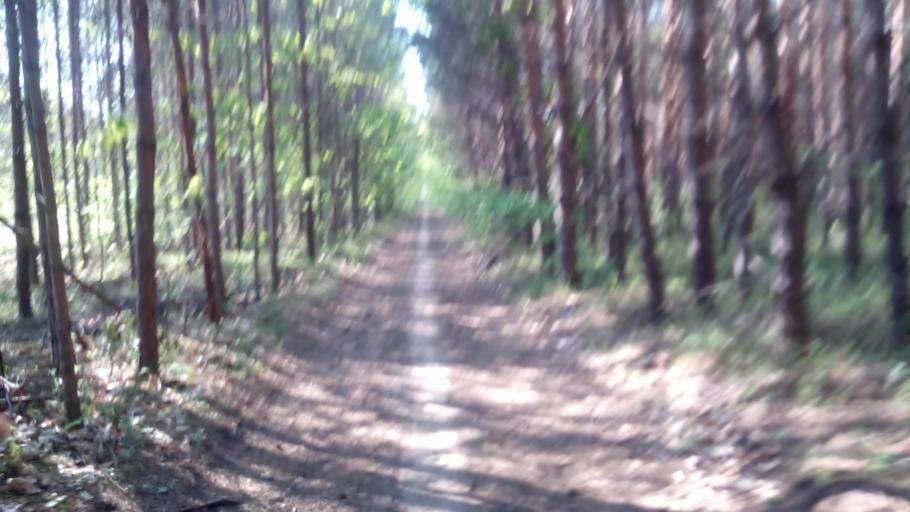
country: PL
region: Opole Voivodeship
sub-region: Powiat opolski
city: Tarnow Opolski
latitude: 50.5874
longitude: 18.0494
